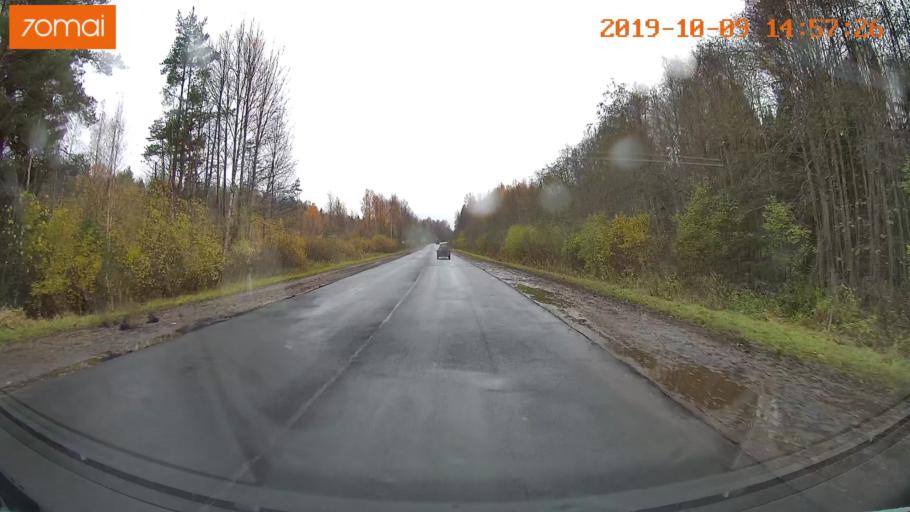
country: RU
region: Kostroma
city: Chistyye Bory
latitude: 58.3376
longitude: 41.6509
